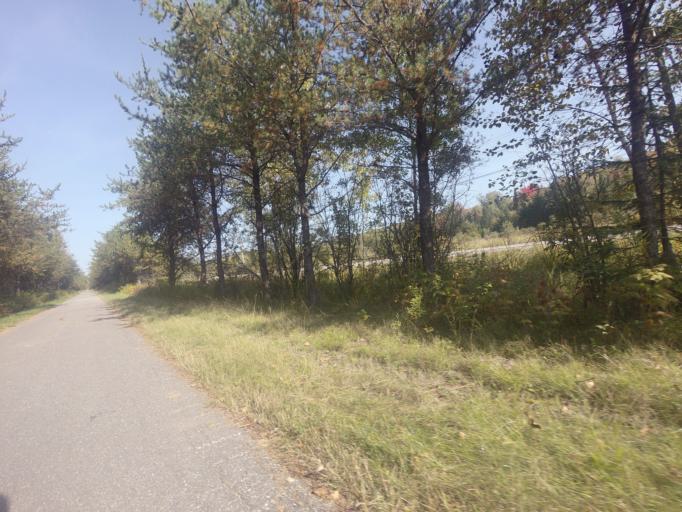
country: CA
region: Quebec
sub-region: Laurentides
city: Mont-Laurier
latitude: 46.5406
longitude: -75.4700
